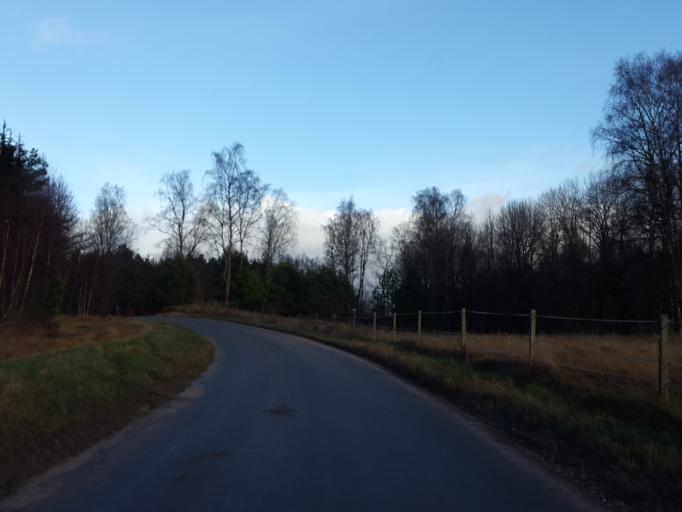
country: SE
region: Vaestra Goetaland
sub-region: Vargarda Kommun
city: Jonstorp
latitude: 57.9730
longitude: 12.7402
